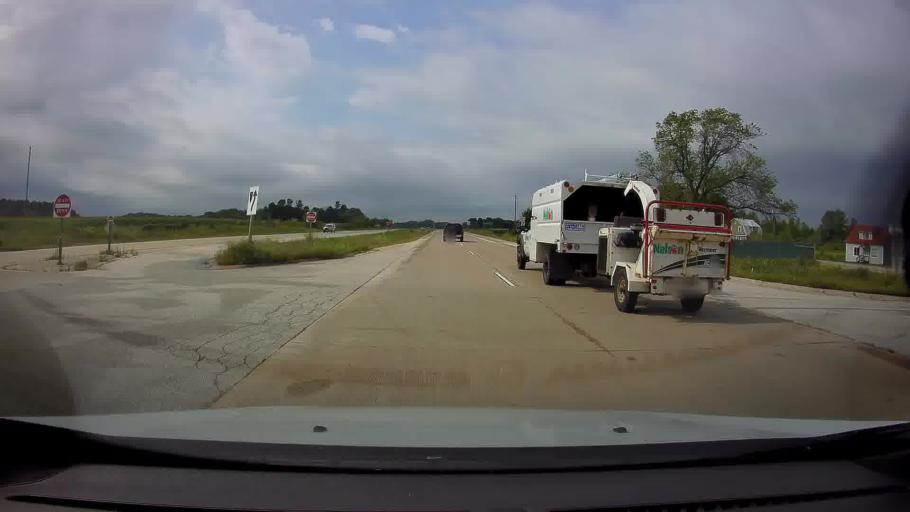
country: US
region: Wisconsin
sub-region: Kewaunee County
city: Luxemburg
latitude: 44.6776
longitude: -87.7299
